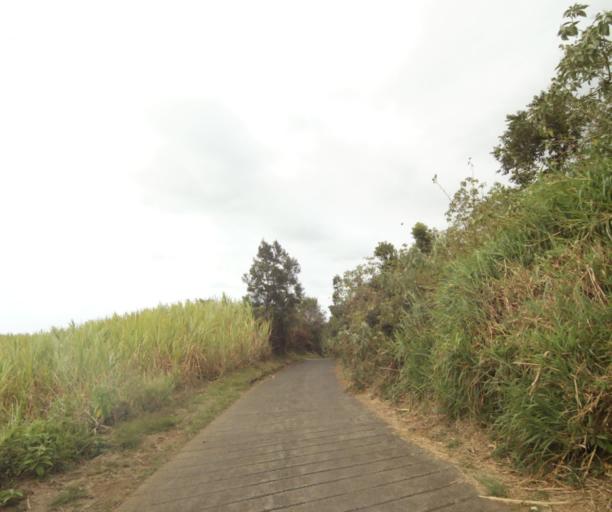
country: RE
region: Reunion
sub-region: Reunion
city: Saint-Paul
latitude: -21.0238
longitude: 55.3224
